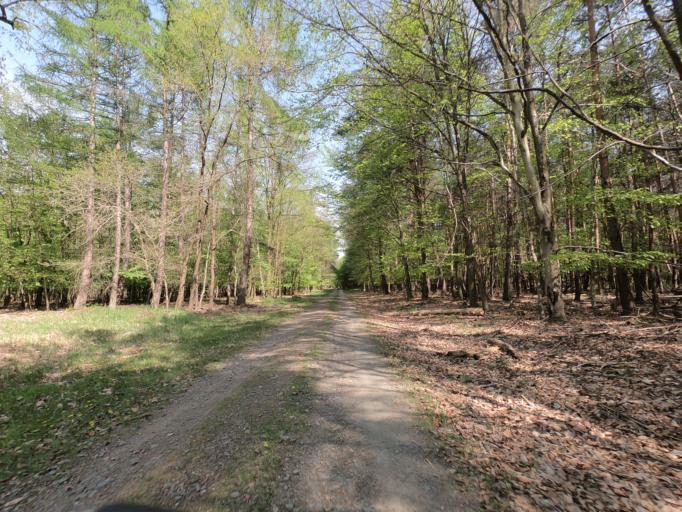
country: DE
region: Hesse
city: Morfelden-Walldorf
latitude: 50.0054
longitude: 8.5480
